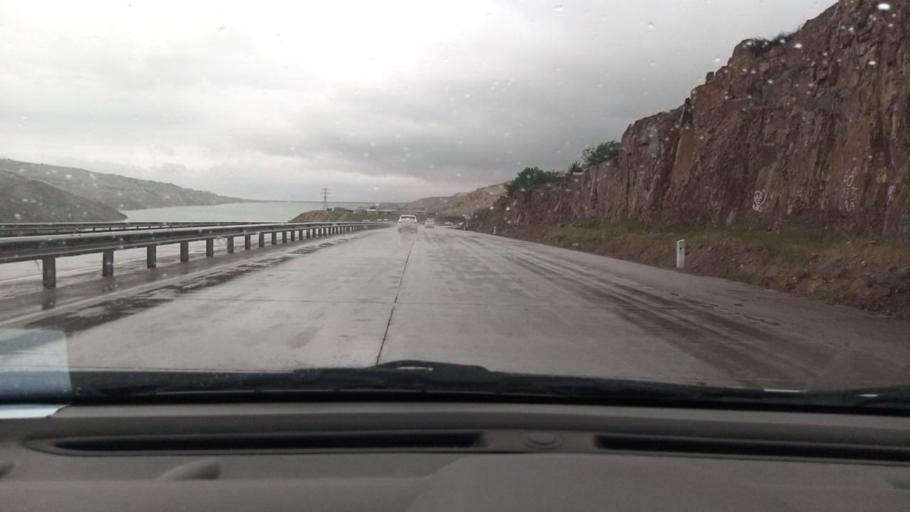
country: UZ
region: Toshkent
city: Angren
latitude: 41.0743
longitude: 70.2594
